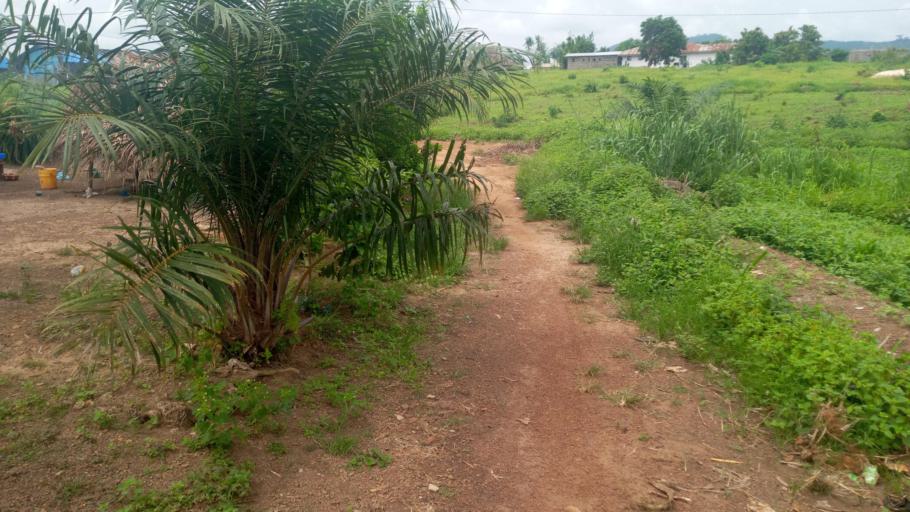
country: SL
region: Southern Province
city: Mogbwemo
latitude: 7.7767
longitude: -12.3034
